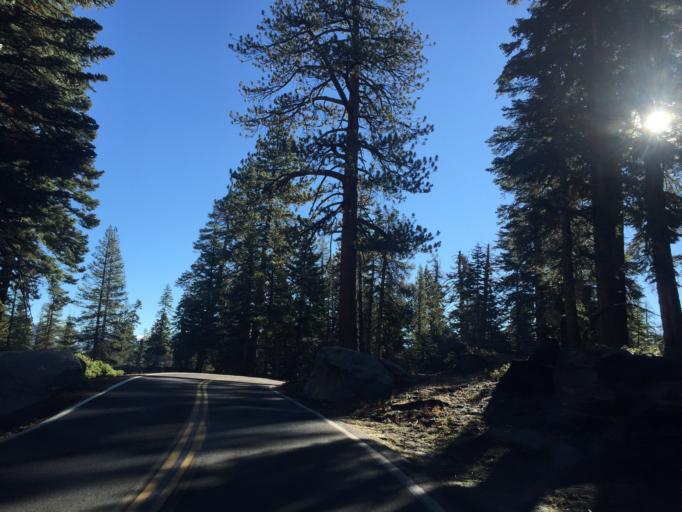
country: US
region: California
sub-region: Mariposa County
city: Yosemite Valley
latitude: 37.7190
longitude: -119.5801
